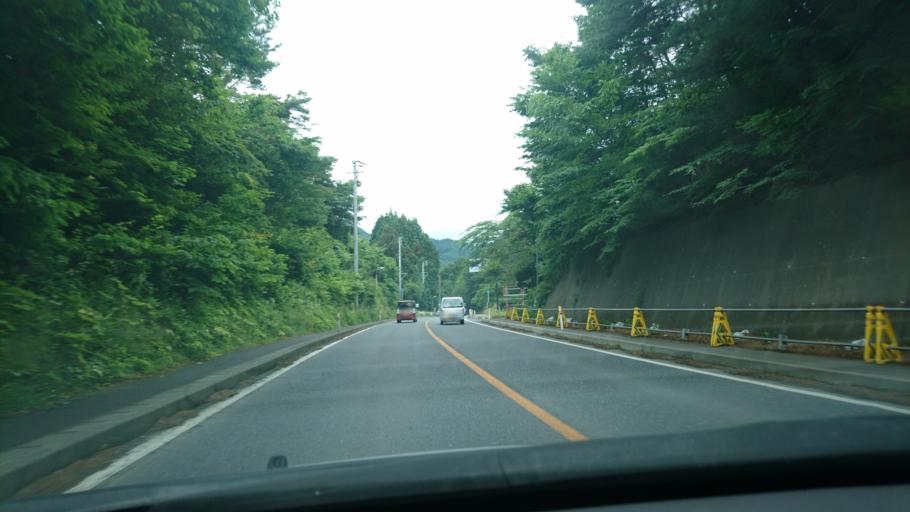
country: JP
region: Iwate
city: Otsuchi
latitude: 39.3766
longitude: 141.9414
